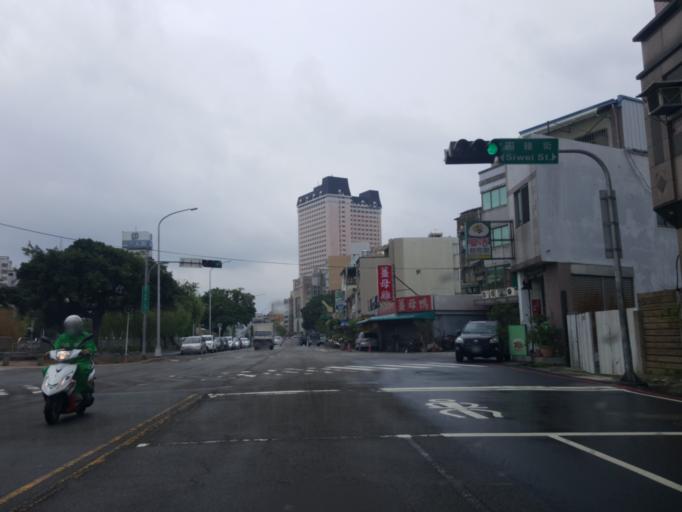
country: TW
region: Taiwan
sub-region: Taichung City
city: Taichung
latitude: 24.1401
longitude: 120.6722
